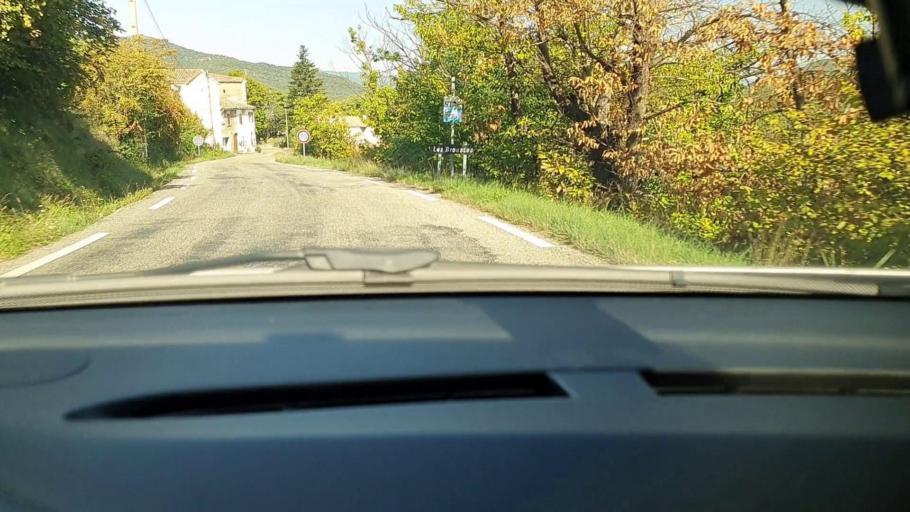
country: FR
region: Languedoc-Roussillon
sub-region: Departement du Gard
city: Saint-Florent-sur-Auzonnet
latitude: 44.2521
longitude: 4.1342
